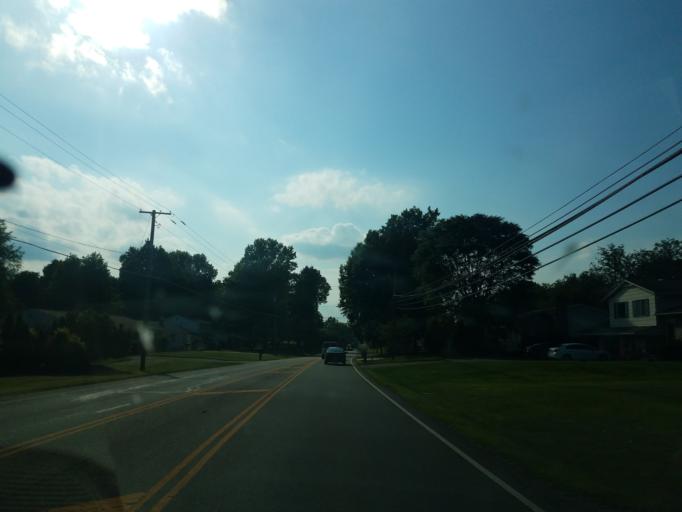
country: US
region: Ohio
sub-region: Stark County
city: Canal Fulton
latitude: 40.8827
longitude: -81.5777
